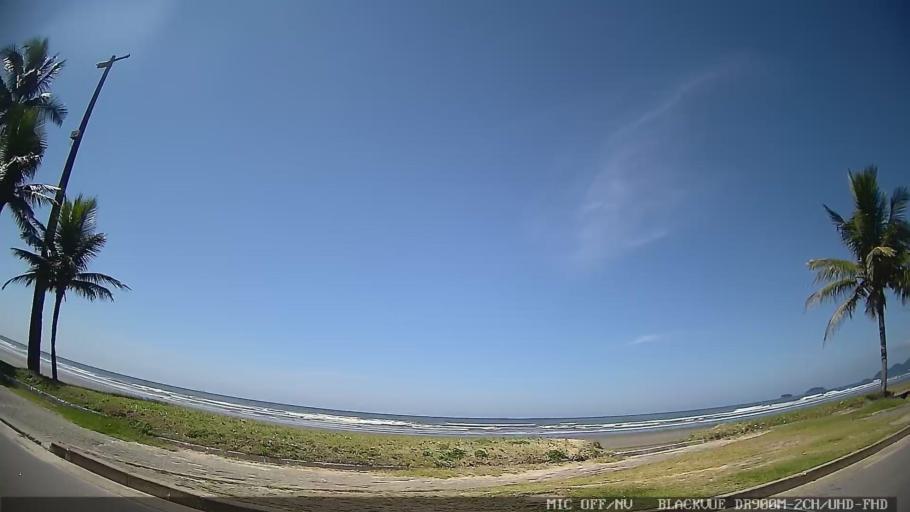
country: BR
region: Sao Paulo
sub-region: Peruibe
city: Peruibe
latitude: -24.3101
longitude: -46.9796
